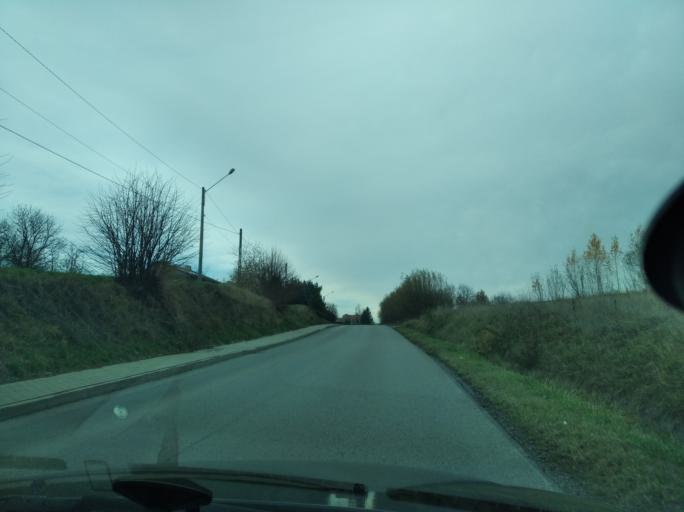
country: PL
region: Subcarpathian Voivodeship
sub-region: Powiat lancucki
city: Albigowa
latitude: 50.0329
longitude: 22.2347
